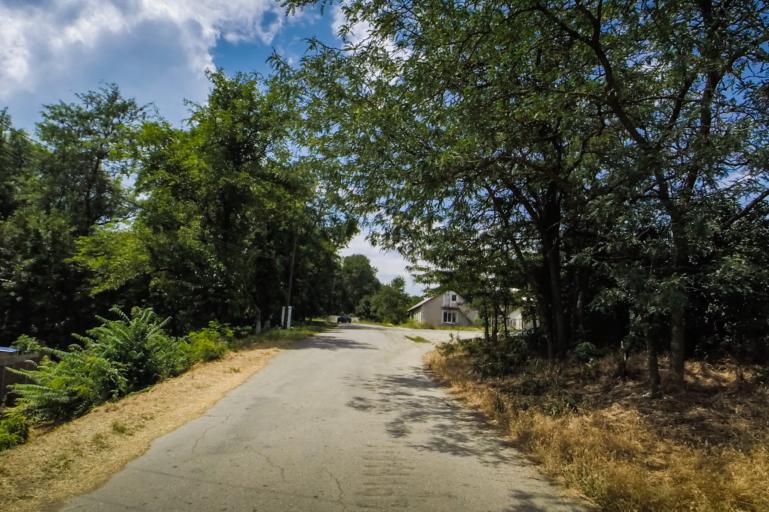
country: RU
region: Kabardino-Balkariya
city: Altud
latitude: 43.7615
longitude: 43.8832
